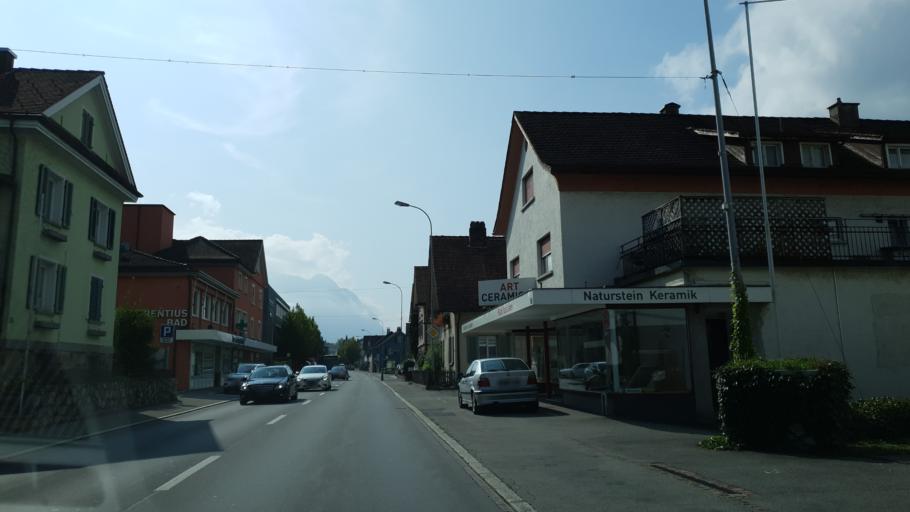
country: LI
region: Schaan
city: Schaan
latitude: 47.1617
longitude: 9.5087
